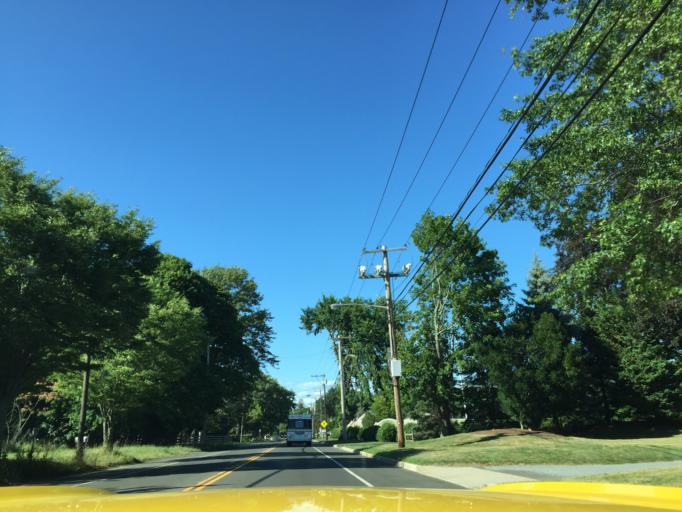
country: US
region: New York
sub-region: Suffolk County
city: Cutchogue
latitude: 41.0138
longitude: -72.4836
